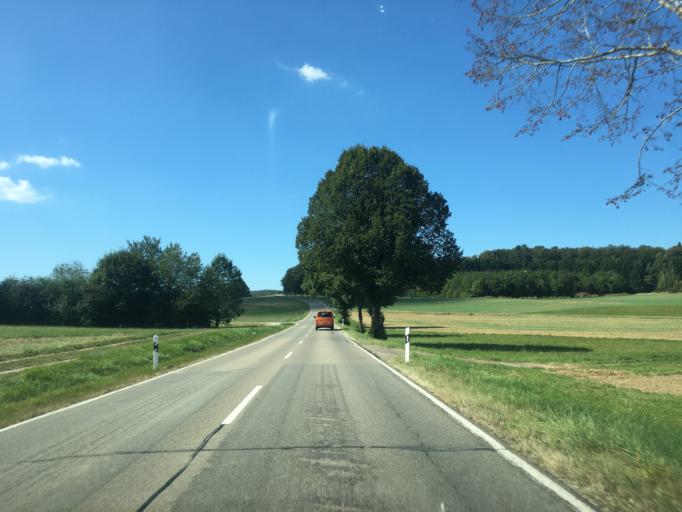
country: DE
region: Baden-Wuerttemberg
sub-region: Tuebingen Region
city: Gomadingen
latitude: 48.3488
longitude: 9.3511
